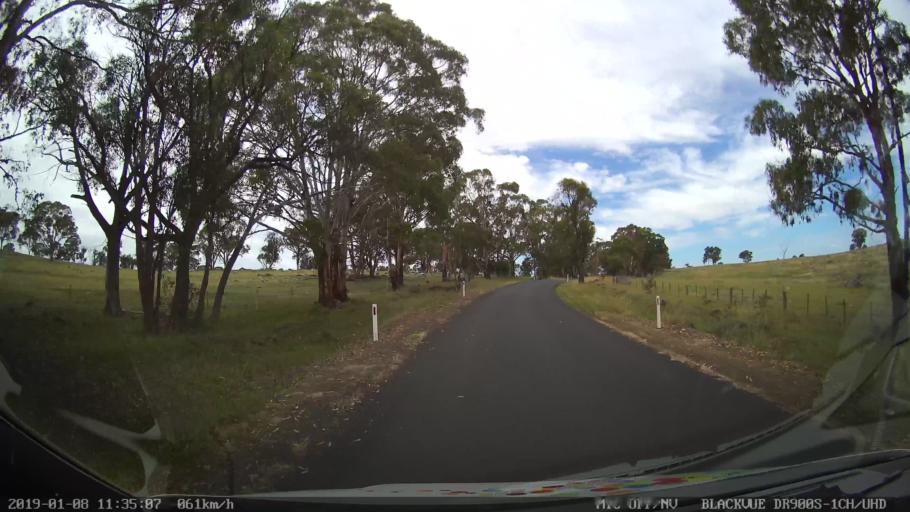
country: AU
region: New South Wales
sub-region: Guyra
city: Guyra
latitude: -30.3341
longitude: 151.5375
